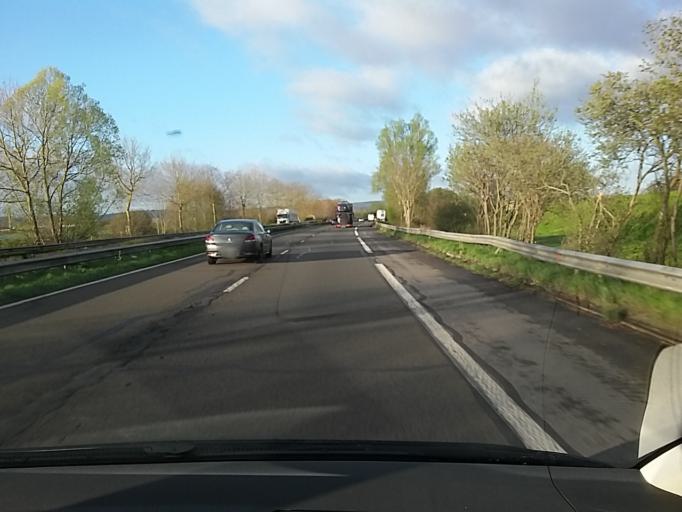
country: FR
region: Picardie
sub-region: Departement de l'Oise
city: Longueil-Sainte-Marie
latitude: 49.3404
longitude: 2.7355
